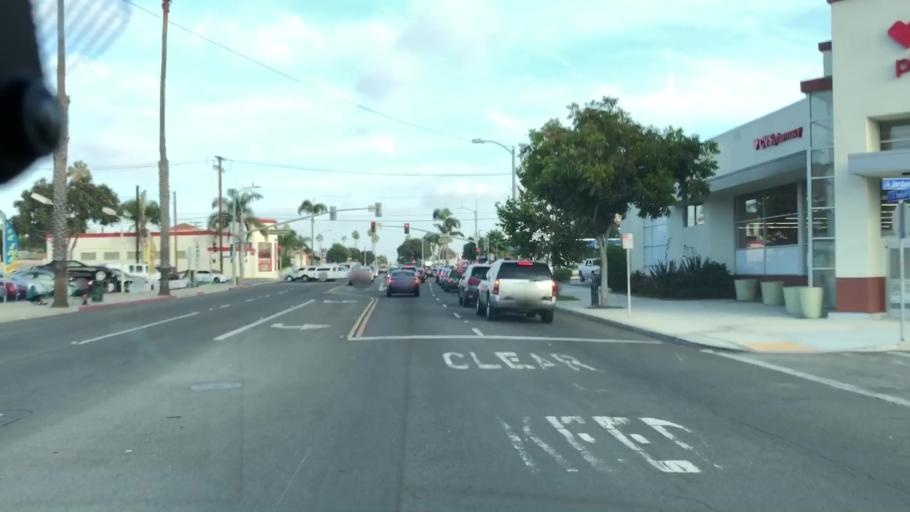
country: US
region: California
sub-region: Ventura County
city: Ventura
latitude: 34.2738
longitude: -119.2674
